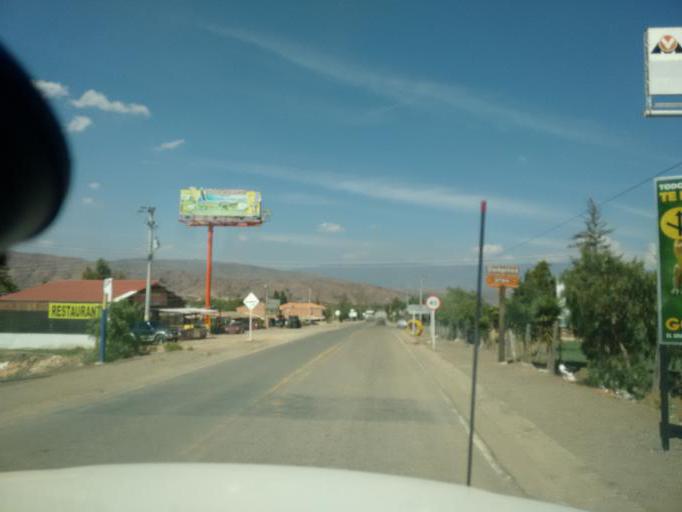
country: CO
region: Boyaca
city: Sachica
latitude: 5.5853
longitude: -73.5311
